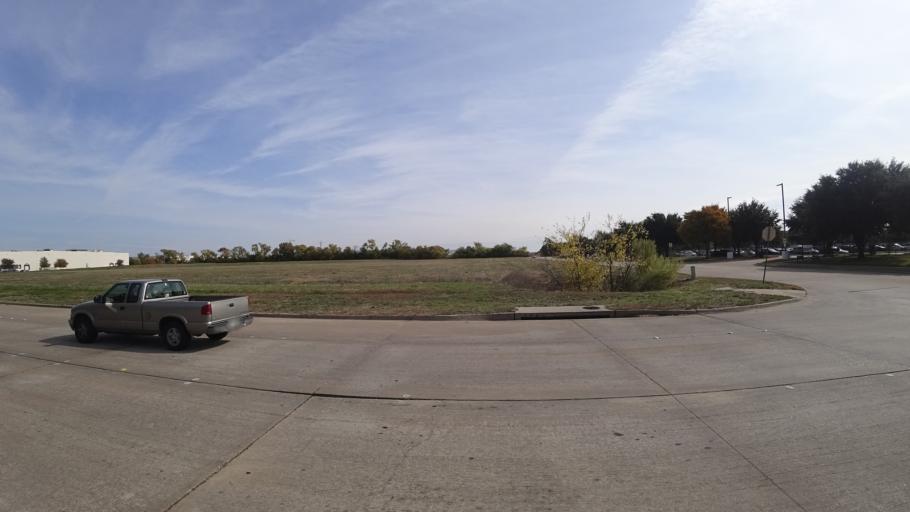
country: US
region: Texas
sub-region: Denton County
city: The Colony
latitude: 33.0661
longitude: -96.8737
